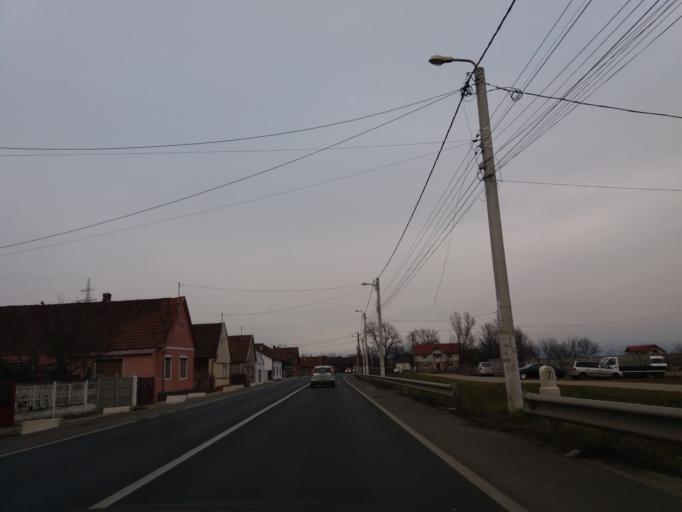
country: RO
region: Hunedoara
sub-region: Comuna Bacia
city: Bacia
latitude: 45.7843
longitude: 23.0009
